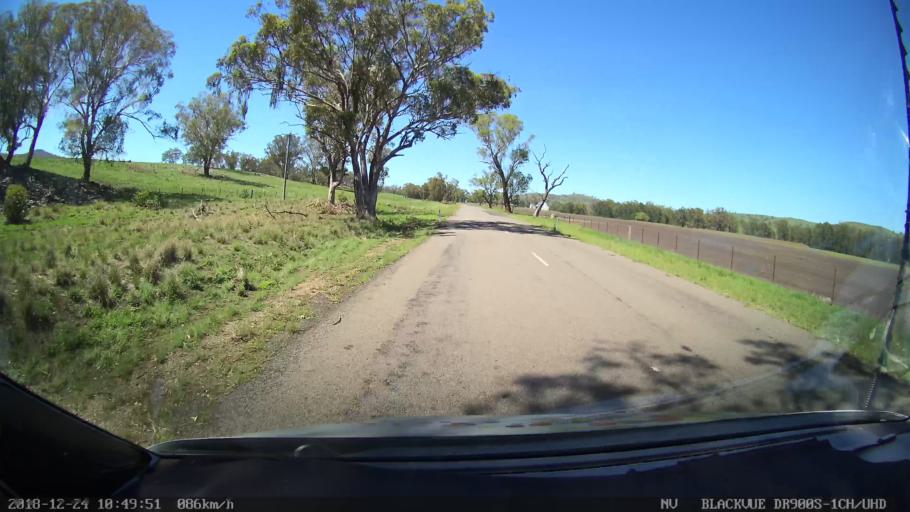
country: AU
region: New South Wales
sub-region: Upper Hunter Shire
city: Merriwa
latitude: -31.9527
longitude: 150.4255
